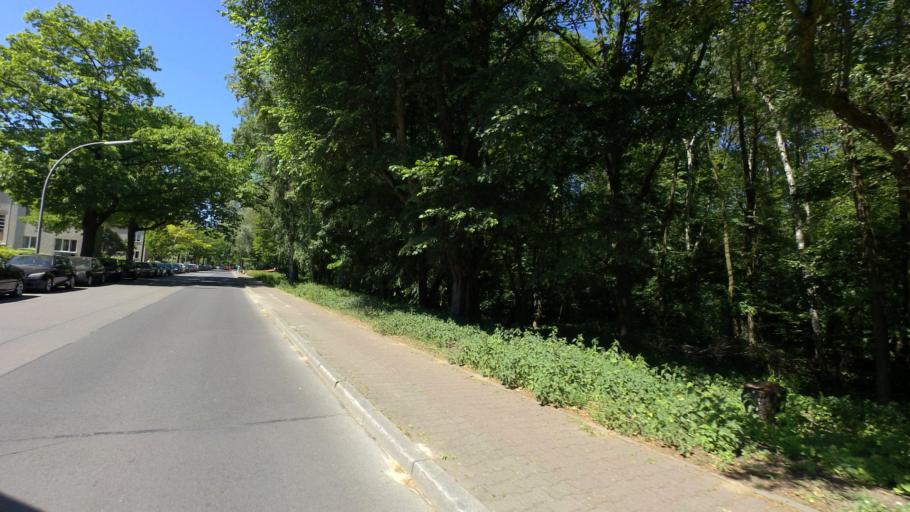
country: DE
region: Berlin
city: Siemensstadt
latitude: 52.5411
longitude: 13.2794
